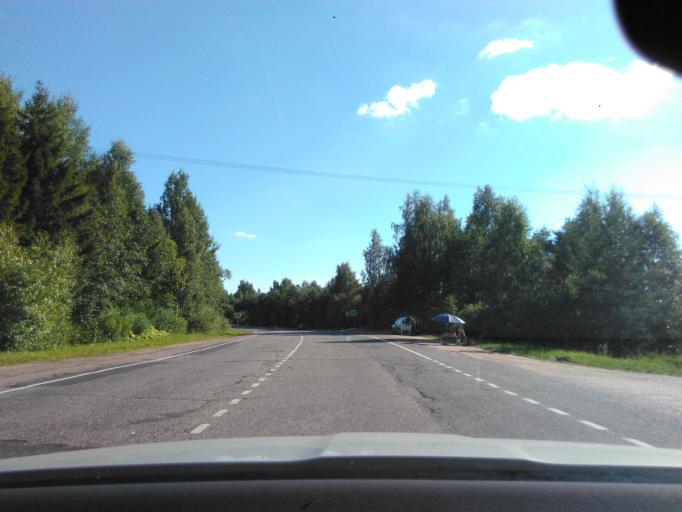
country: RU
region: Tverskaya
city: Konakovo
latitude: 56.6523
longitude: 36.7095
